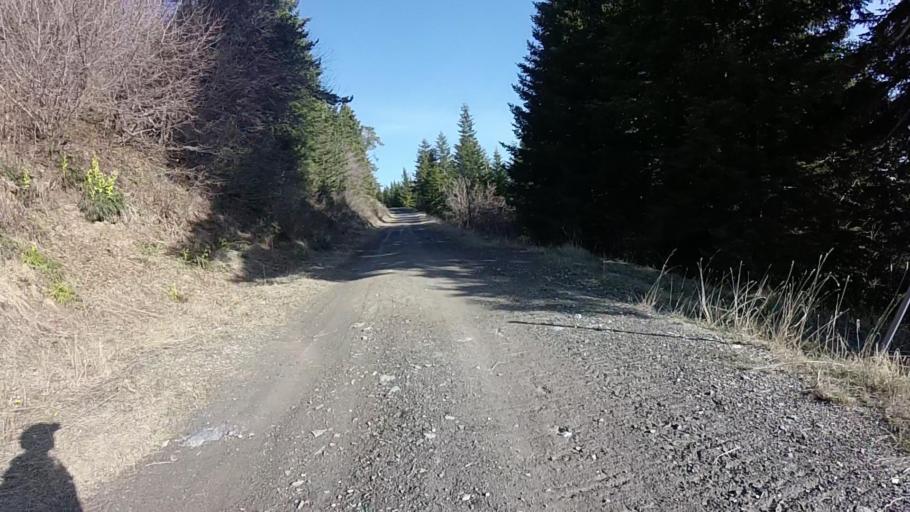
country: FR
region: Provence-Alpes-Cote d'Azur
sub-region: Departement des Alpes-de-Haute-Provence
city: Seyne-les-Alpes
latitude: 44.3462
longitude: 6.2867
